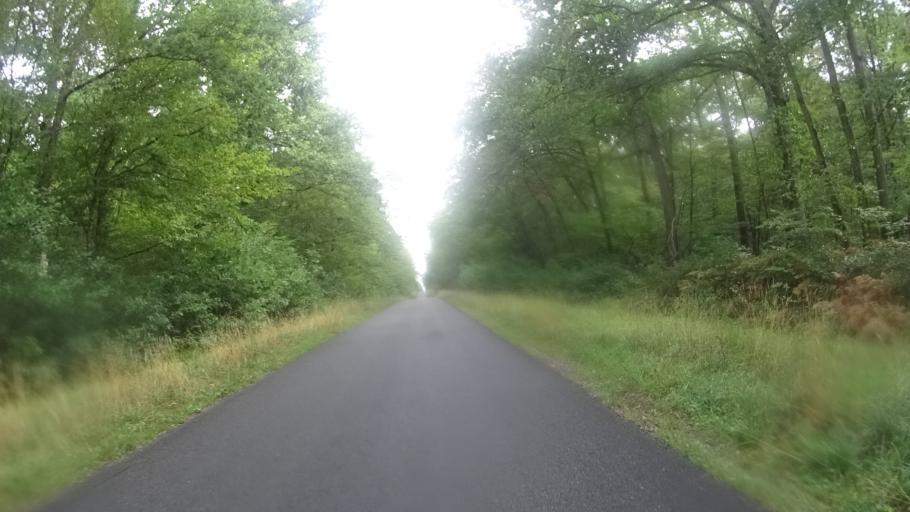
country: FR
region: Centre
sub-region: Departement du Loiret
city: Vitry-aux-Loges
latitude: 48.0203
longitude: 2.2556
